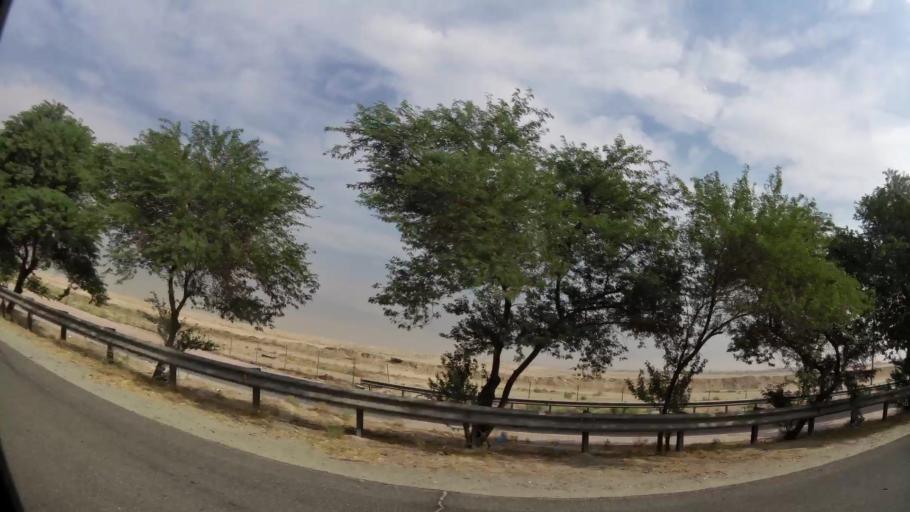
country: KW
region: Muhafazat al Jahra'
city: Al Jahra'
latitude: 29.2887
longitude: 47.7684
